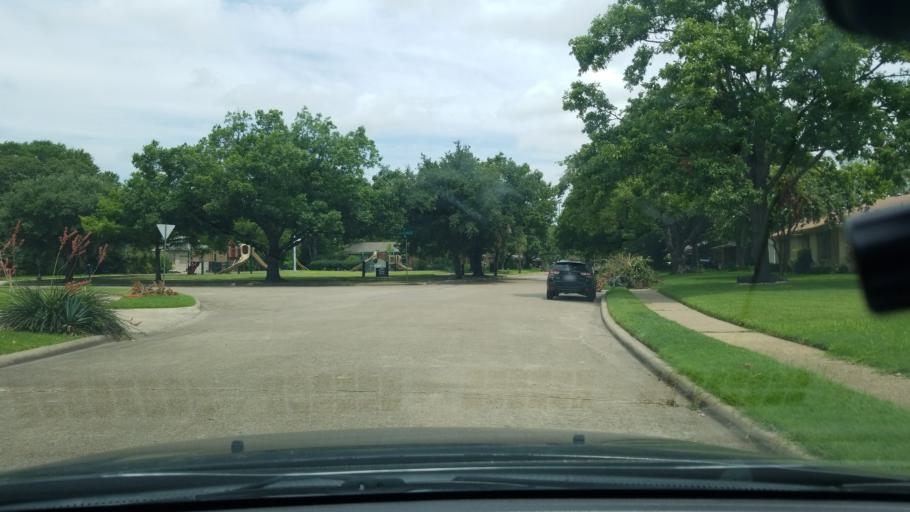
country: US
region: Texas
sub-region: Dallas County
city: Garland
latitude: 32.8291
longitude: -96.6901
